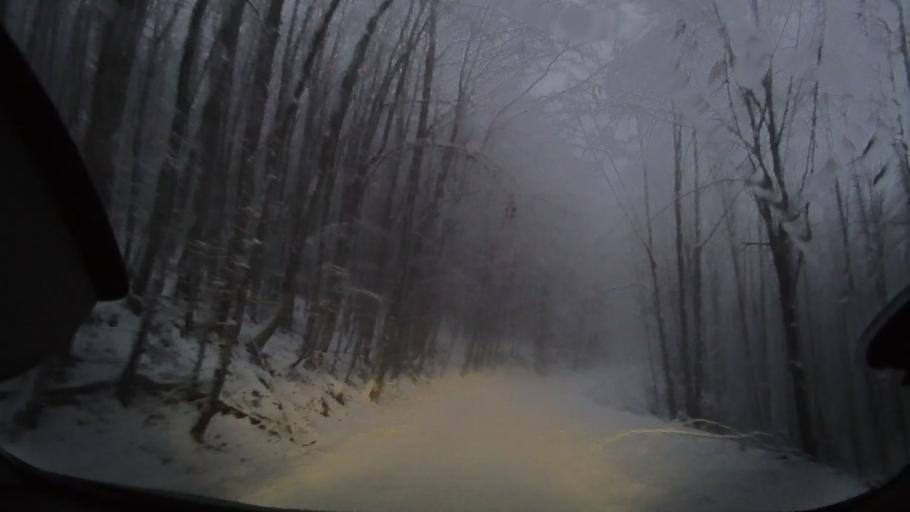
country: RO
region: Alba
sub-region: Comuna Avram Iancu
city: Avram Iancu
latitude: 46.3147
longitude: 22.8168
